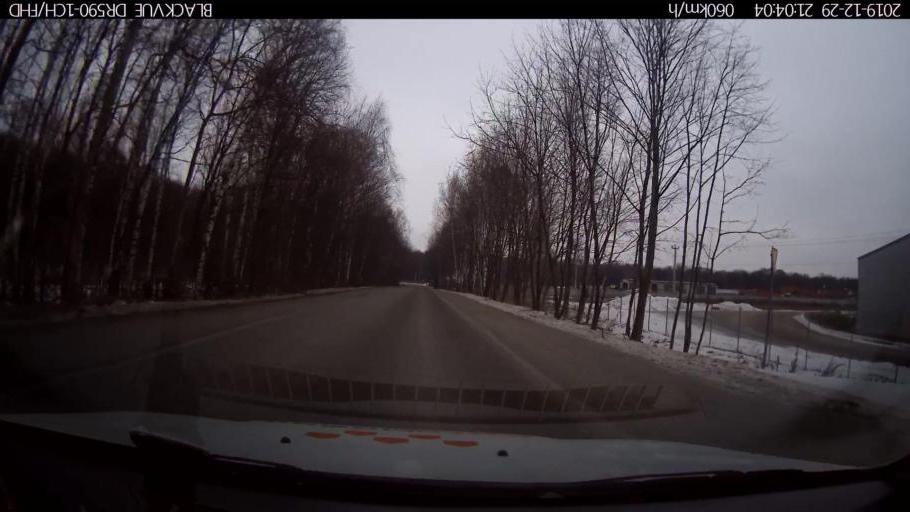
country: RU
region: Nizjnij Novgorod
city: Afonino
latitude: 56.2004
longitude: 44.0039
